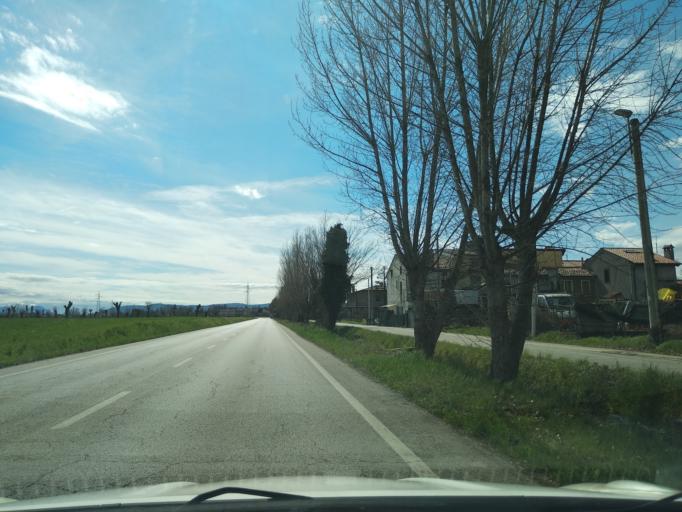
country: IT
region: Veneto
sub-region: Provincia di Vicenza
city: Monticello Conte Otto
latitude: 45.5872
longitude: 11.5789
